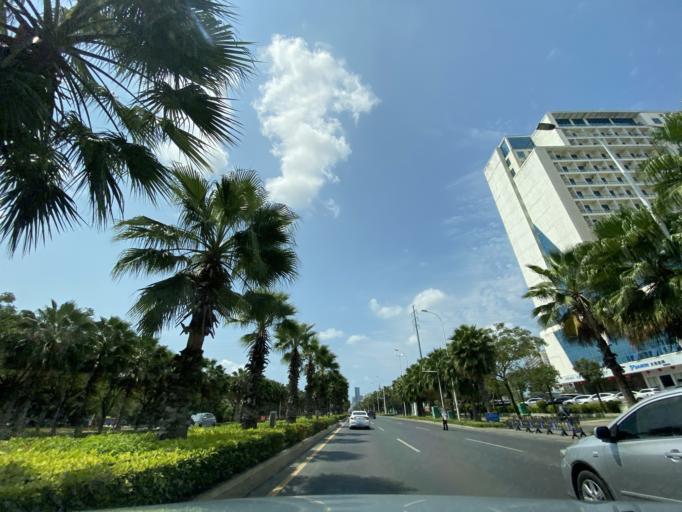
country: CN
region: Hainan
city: Sanya
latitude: 18.2884
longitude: 109.5223
